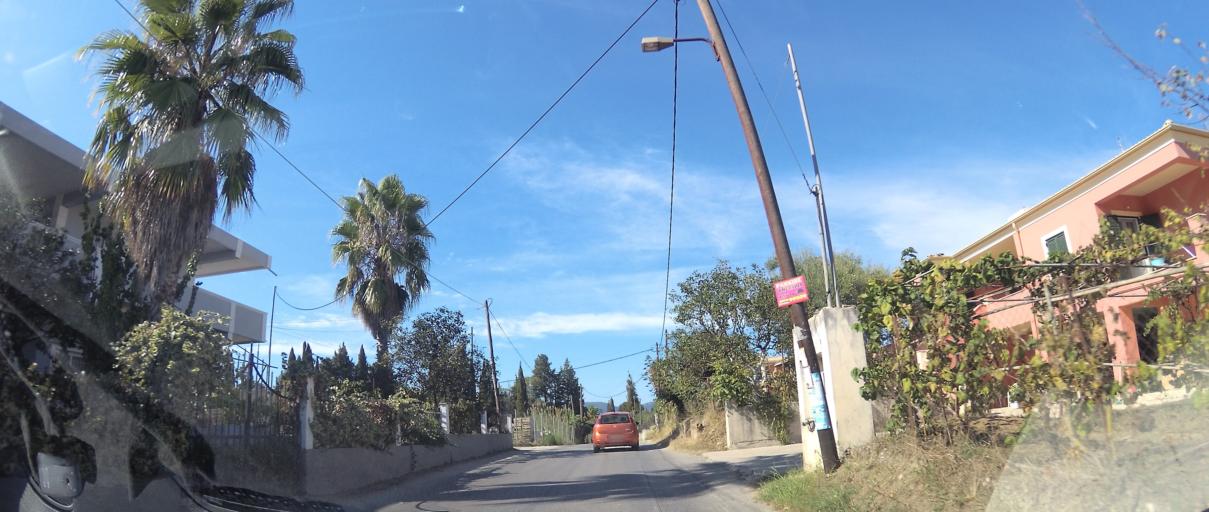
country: GR
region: Ionian Islands
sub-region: Nomos Kerkyras
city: Kontokali
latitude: 39.6471
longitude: 19.8448
